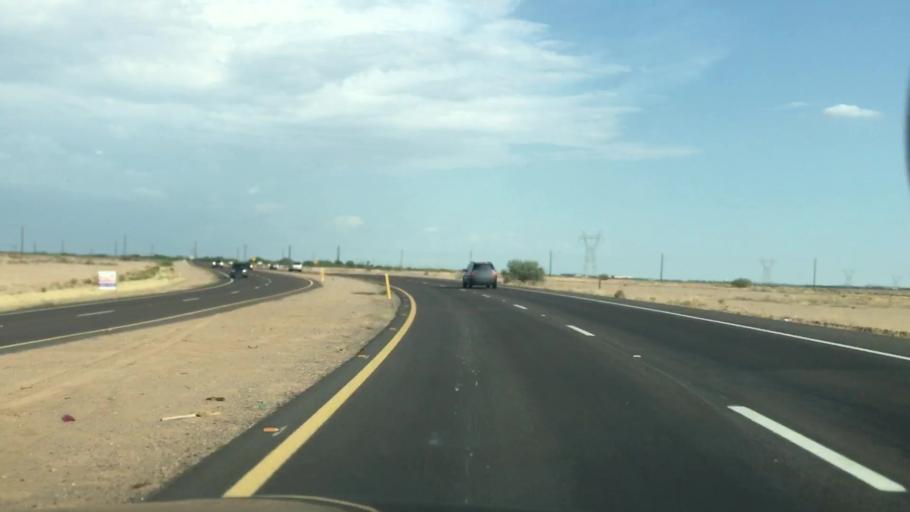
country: US
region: Arizona
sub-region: Pinal County
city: San Tan Valley
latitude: 33.1955
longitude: -111.5634
